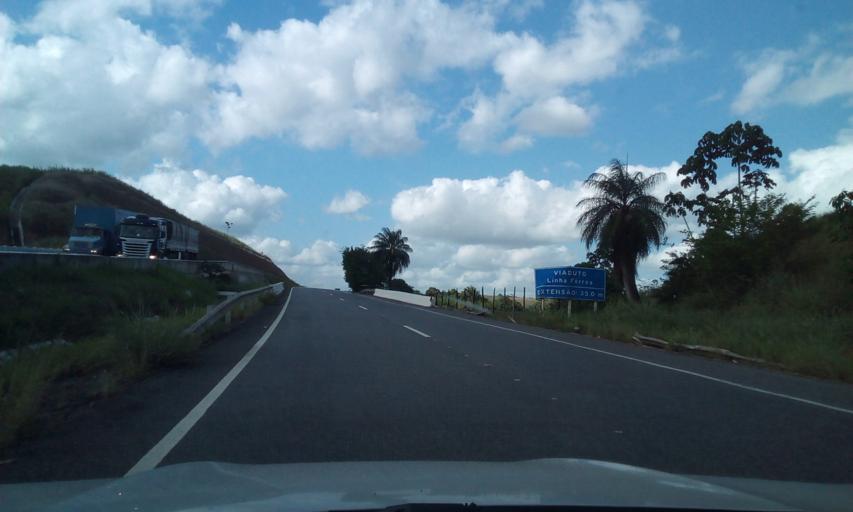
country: BR
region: Alagoas
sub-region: Novo Lino
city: Novo Lino
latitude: -8.8759
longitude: -35.6291
